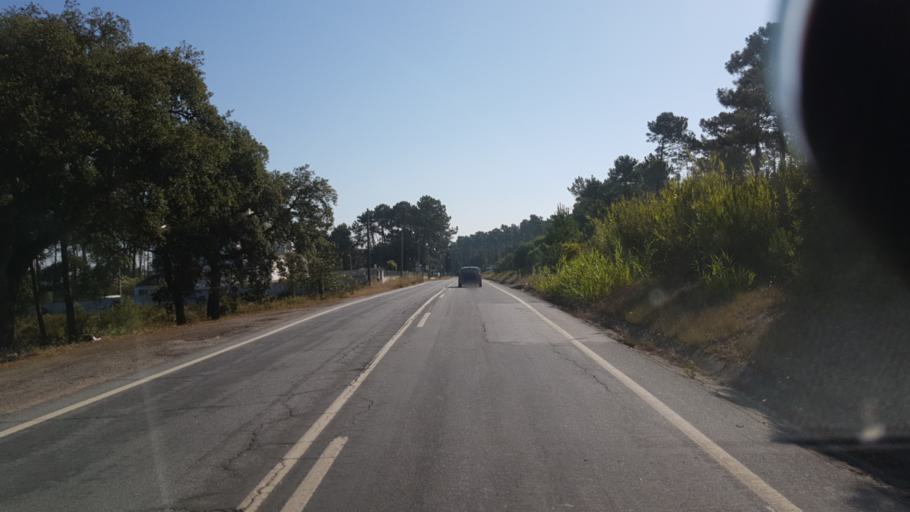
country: PT
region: Setubal
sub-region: Sesimbra
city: Sesimbra
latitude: 38.4864
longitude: -9.0642
